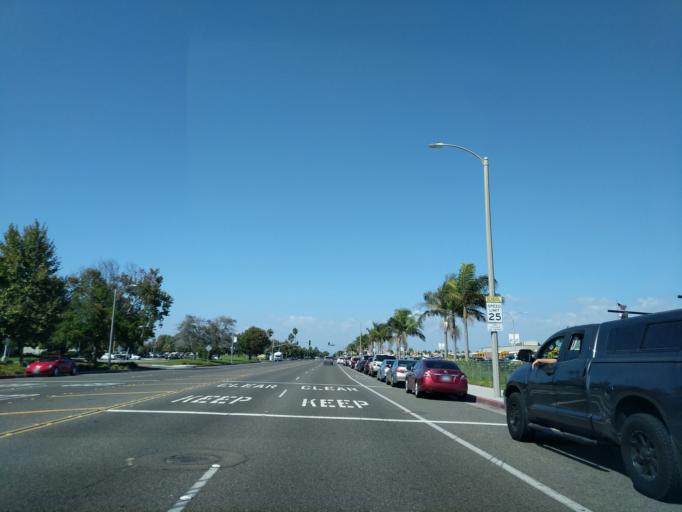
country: US
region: California
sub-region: Orange County
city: Huntington Beach
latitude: 33.6511
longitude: -117.9709
